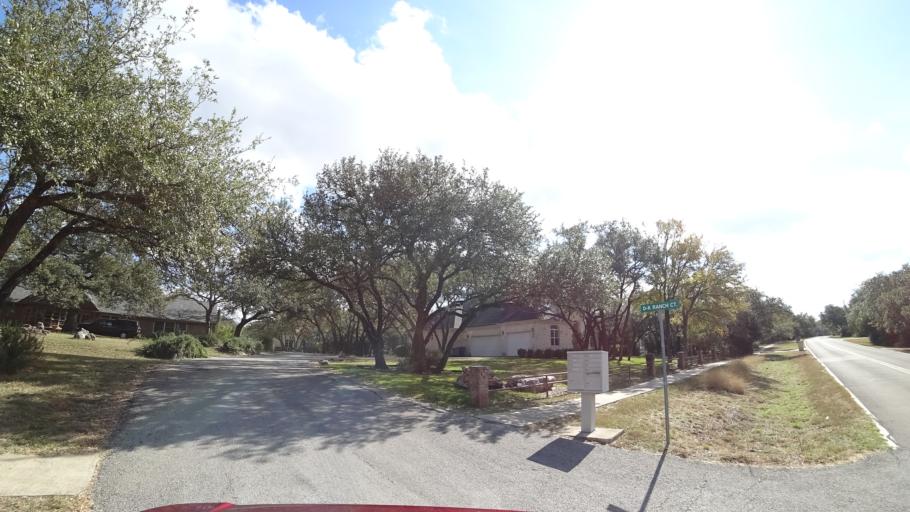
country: US
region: Texas
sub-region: Williamson County
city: Jollyville
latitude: 30.4199
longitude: -97.7807
